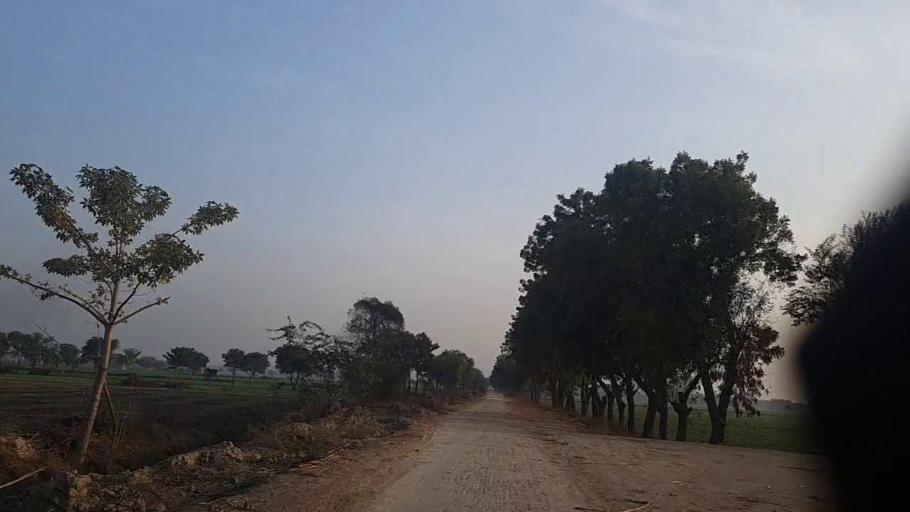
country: PK
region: Sindh
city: Sakrand
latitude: 26.1234
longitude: 68.2306
